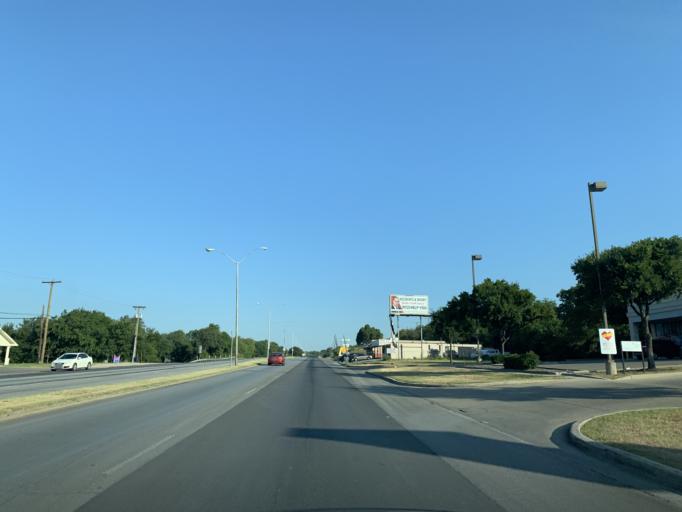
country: US
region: Texas
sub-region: Tarrant County
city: River Oaks
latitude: 32.7892
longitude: -97.3875
